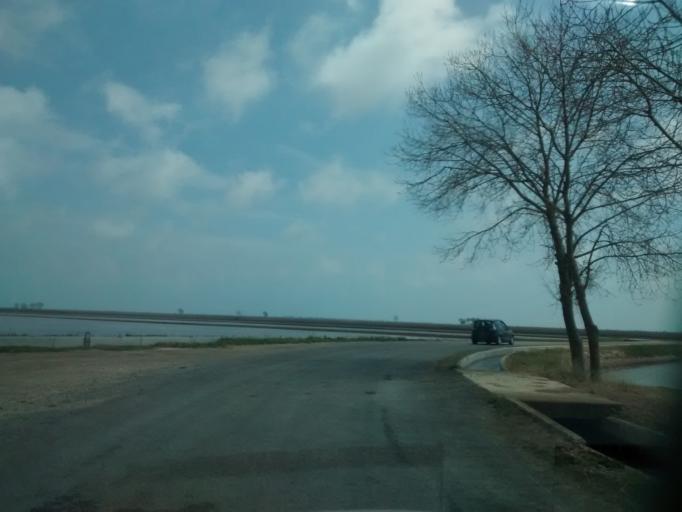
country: ES
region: Catalonia
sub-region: Provincia de Tarragona
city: Deltebre
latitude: 40.6830
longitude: 0.7947
